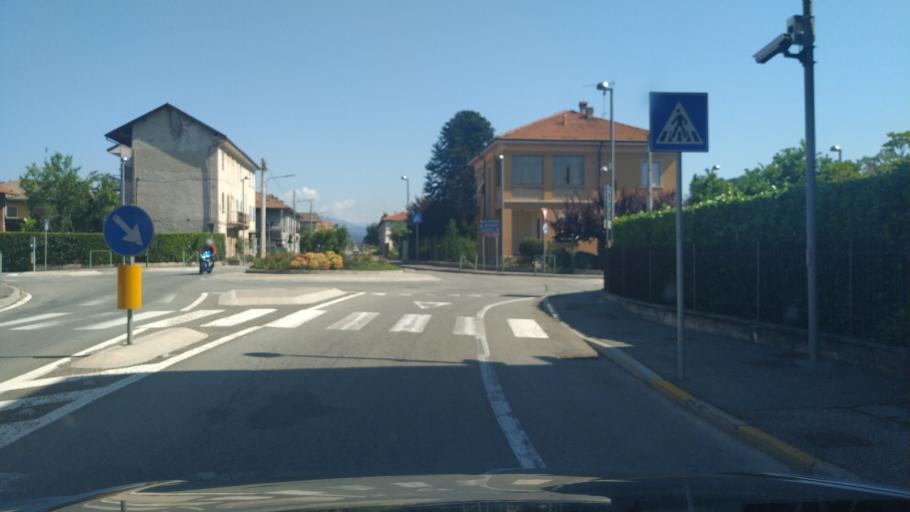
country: IT
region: Piedmont
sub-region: Provincia di Novara
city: Cureggio
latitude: 45.6740
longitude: 8.4559
